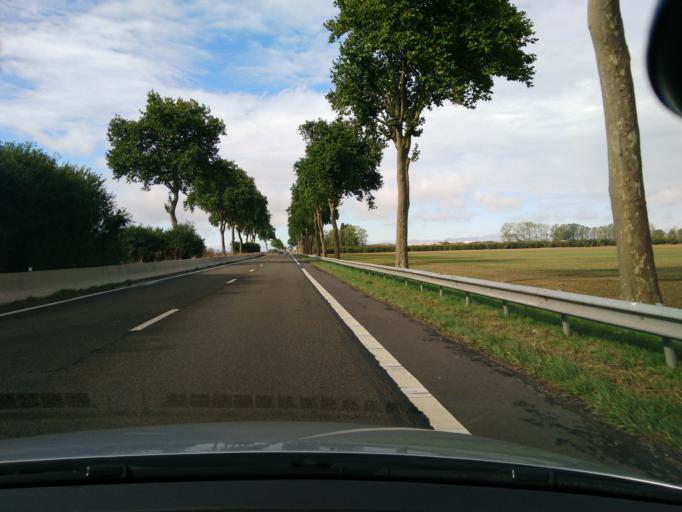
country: FR
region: Centre
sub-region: Departement d'Eure-et-Loir
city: Bu
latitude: 48.7601
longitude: 1.4997
